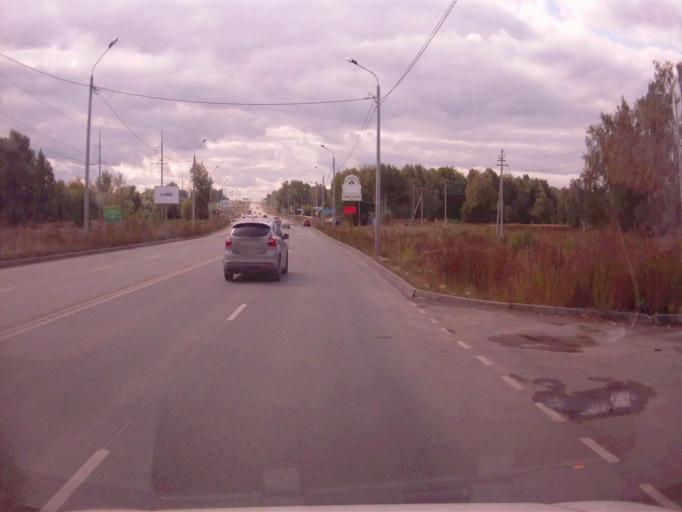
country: RU
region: Chelyabinsk
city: Sargazy
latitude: 55.1457
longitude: 61.2870
